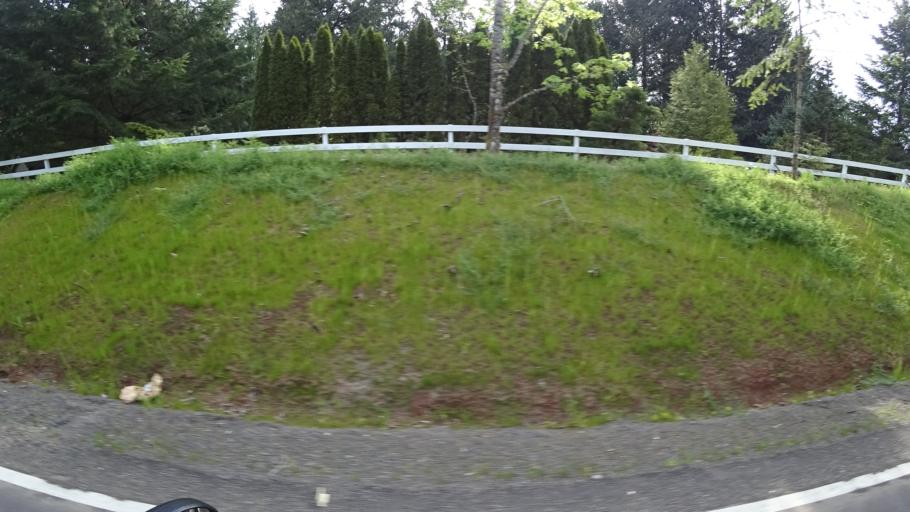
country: US
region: Oregon
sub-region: Washington County
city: Aloha
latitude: 45.4463
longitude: -122.8568
